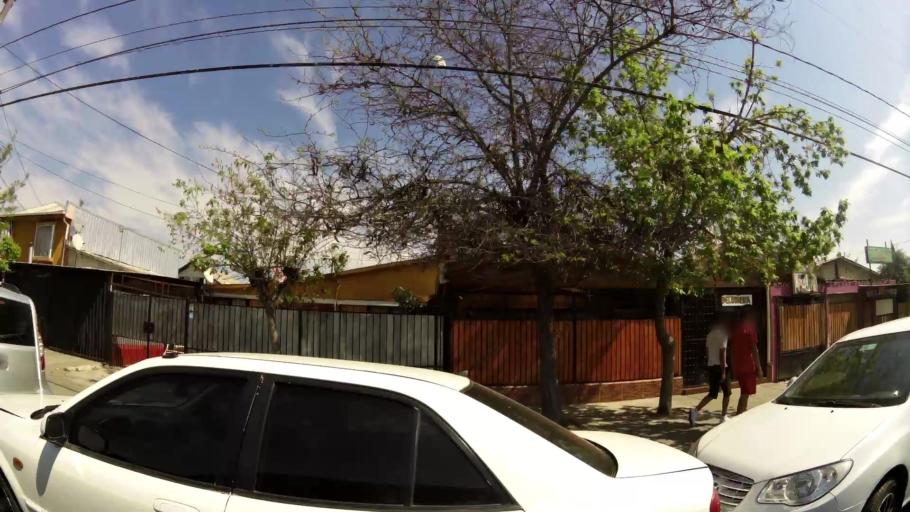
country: CL
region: Santiago Metropolitan
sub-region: Provincia de Santiago
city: La Pintana
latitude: -33.5579
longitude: -70.6377
